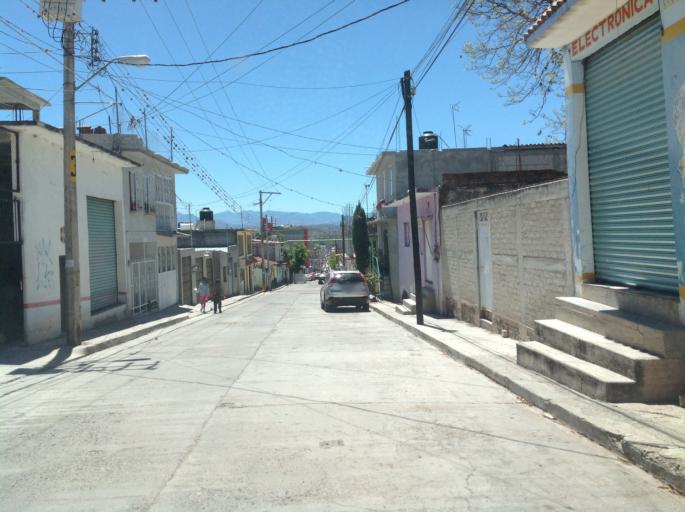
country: MX
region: Oaxaca
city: Ciudad de Huajuapam de Leon
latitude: 17.8132
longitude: -97.7743
